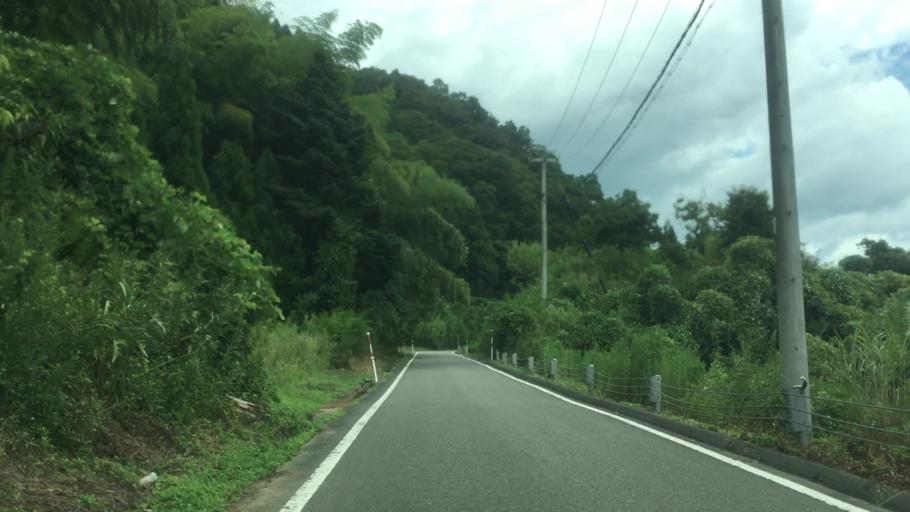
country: JP
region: Hyogo
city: Toyooka
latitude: 35.5824
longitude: 134.7990
